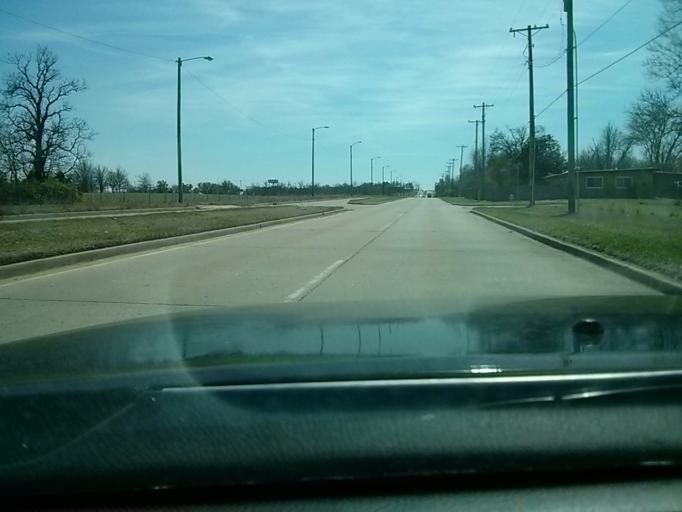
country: US
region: Oklahoma
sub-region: Tulsa County
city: Owasso
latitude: 36.1740
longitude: -95.8868
